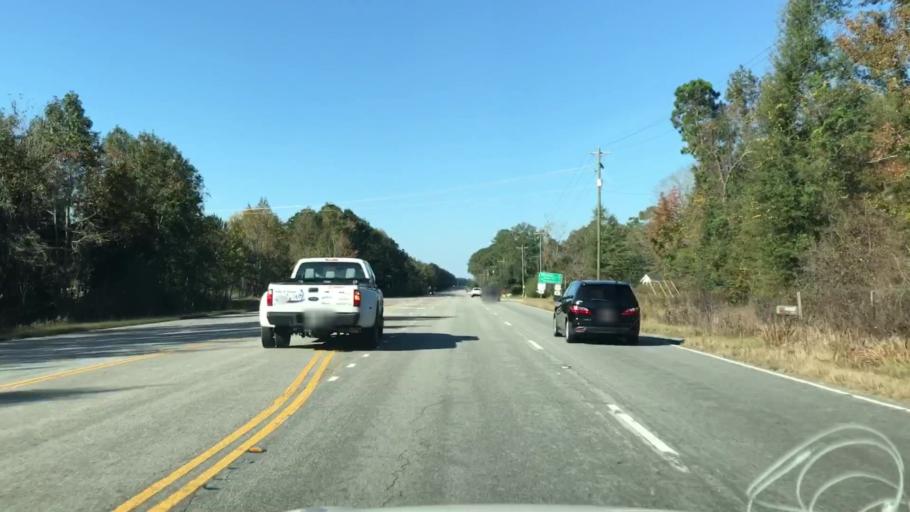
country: US
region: South Carolina
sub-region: Charleston County
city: Ravenel
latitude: 32.7555
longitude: -80.3450
